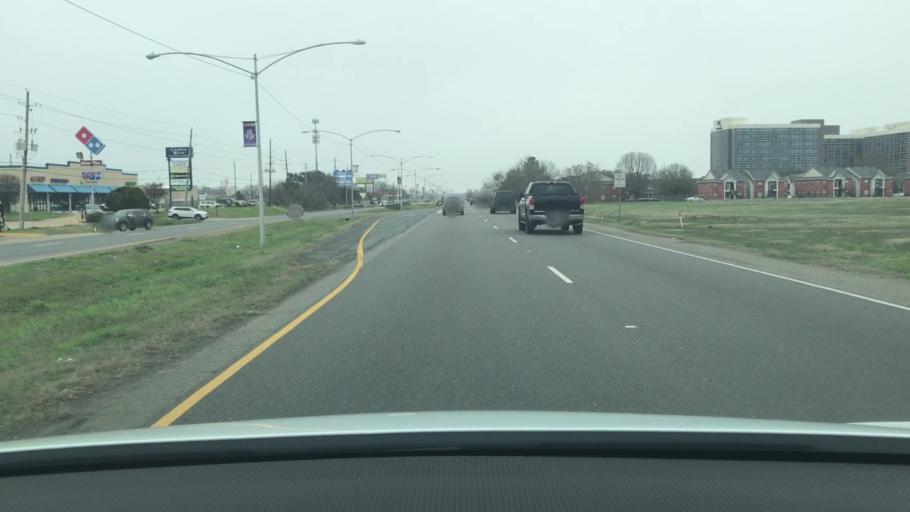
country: US
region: Louisiana
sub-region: Bossier Parish
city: Bossier City
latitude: 32.4270
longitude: -93.7090
